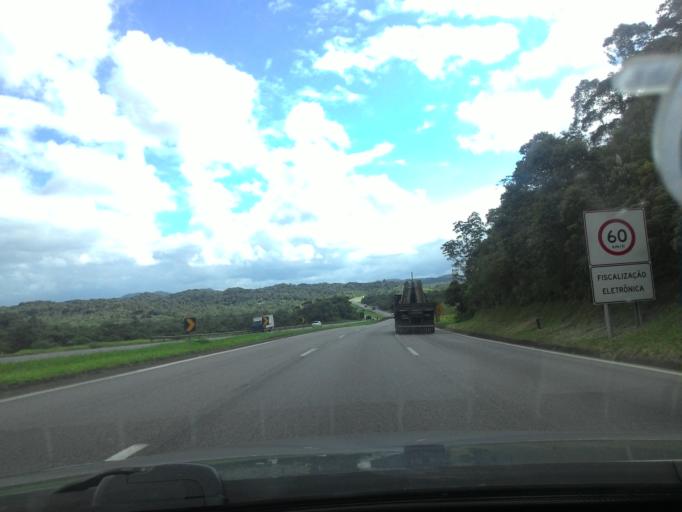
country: BR
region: Sao Paulo
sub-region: Cajati
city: Cajati
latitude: -24.9138
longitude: -48.2540
